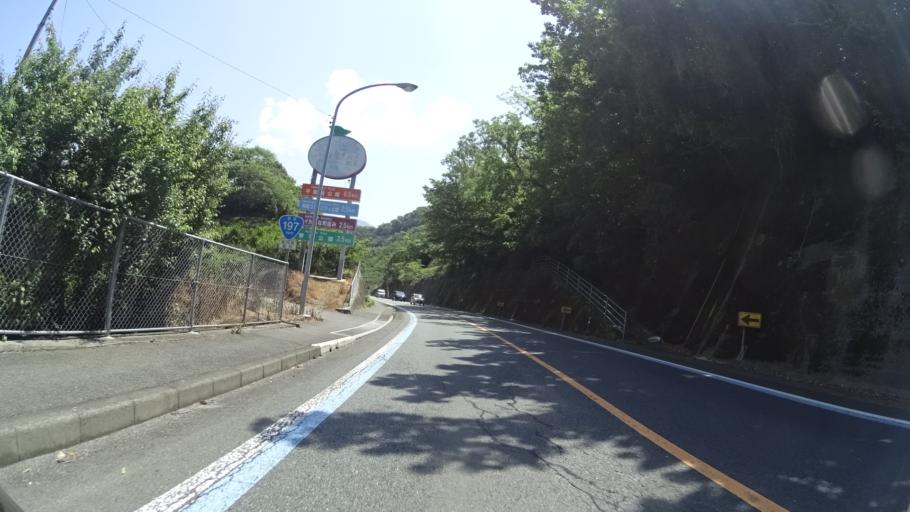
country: JP
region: Ehime
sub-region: Nishiuwa-gun
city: Ikata-cho
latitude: 33.4891
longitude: 132.3883
